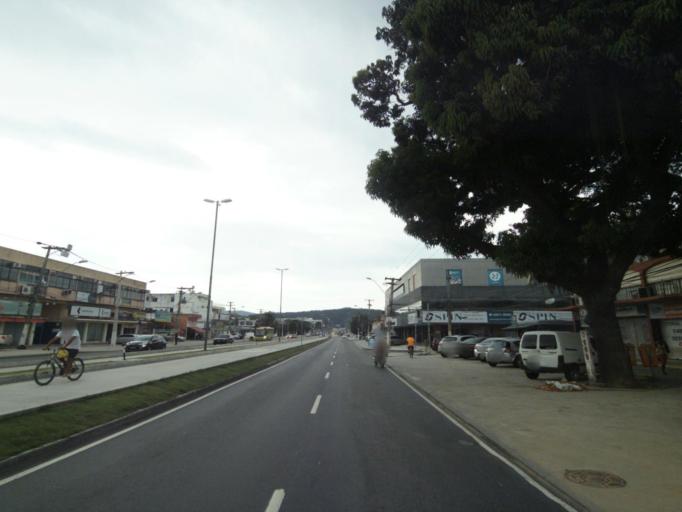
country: BR
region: Rio de Janeiro
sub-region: Niteroi
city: Niteroi
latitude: -22.9356
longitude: -43.0639
